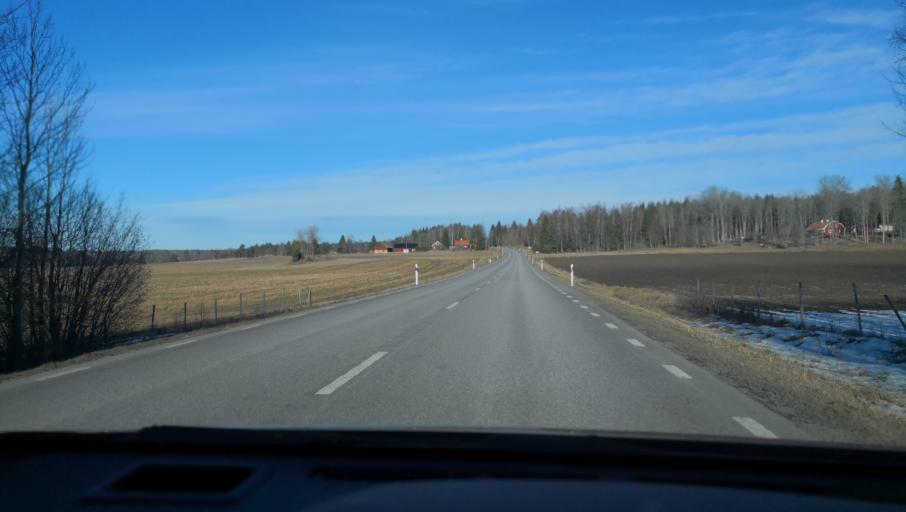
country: SE
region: Uppsala
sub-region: Uppsala Kommun
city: Vattholma
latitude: 60.0600
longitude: 17.7549
